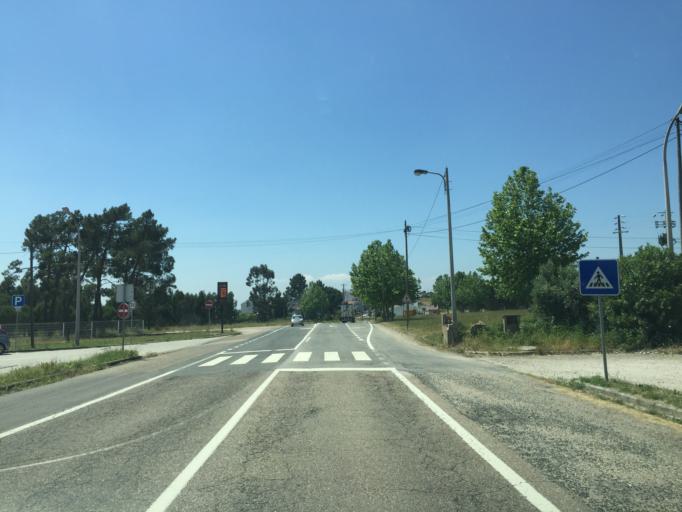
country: PT
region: Santarem
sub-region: Constancia
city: Constancia
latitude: 39.4821
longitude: -8.2880
